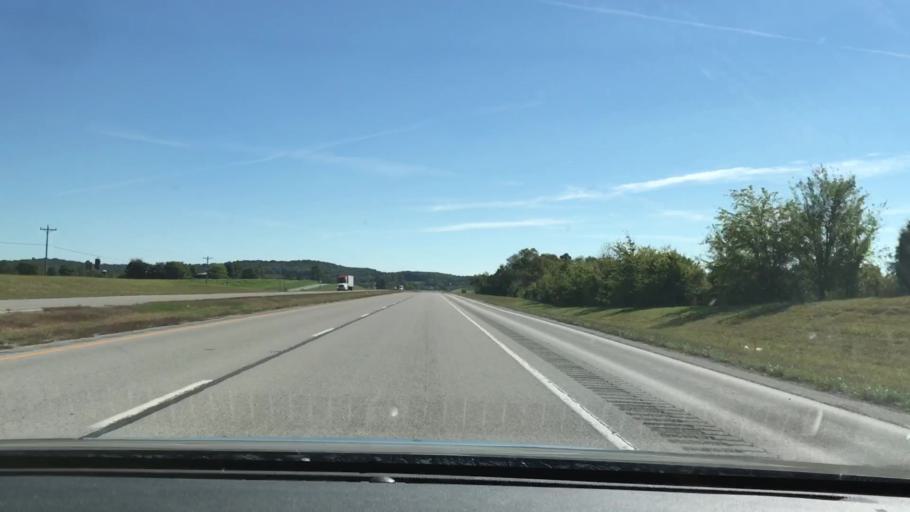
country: US
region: Kentucky
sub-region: Todd County
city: Elkton
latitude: 36.8413
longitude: -87.2587
